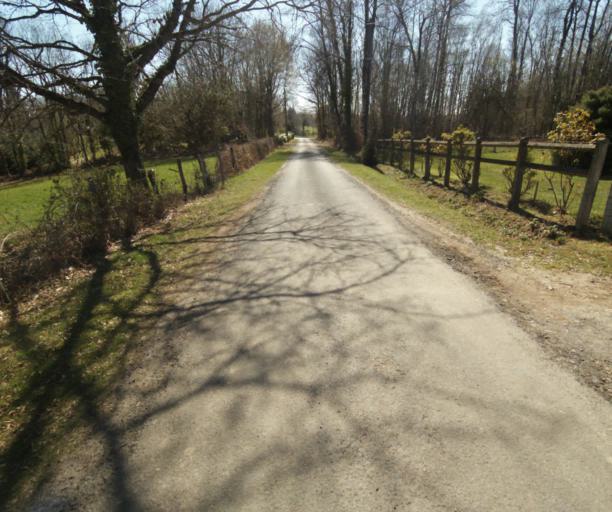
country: FR
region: Limousin
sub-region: Departement de la Correze
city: Saint-Clement
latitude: 45.3239
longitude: 1.6529
